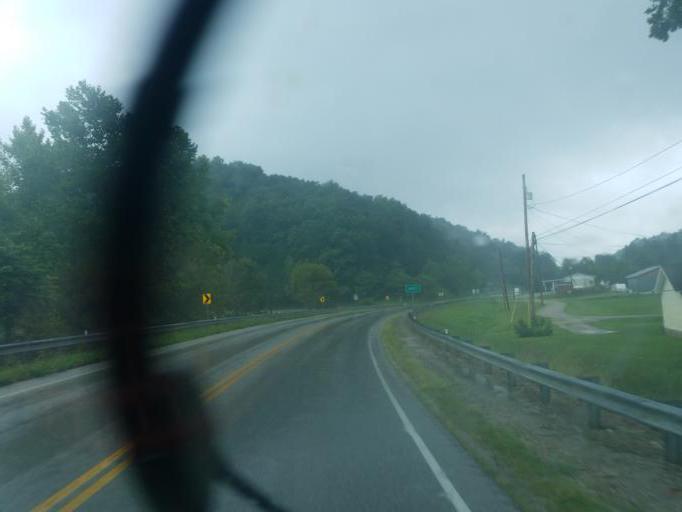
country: US
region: Kentucky
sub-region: Rowan County
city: Morehead
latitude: 38.2321
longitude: -83.3750
